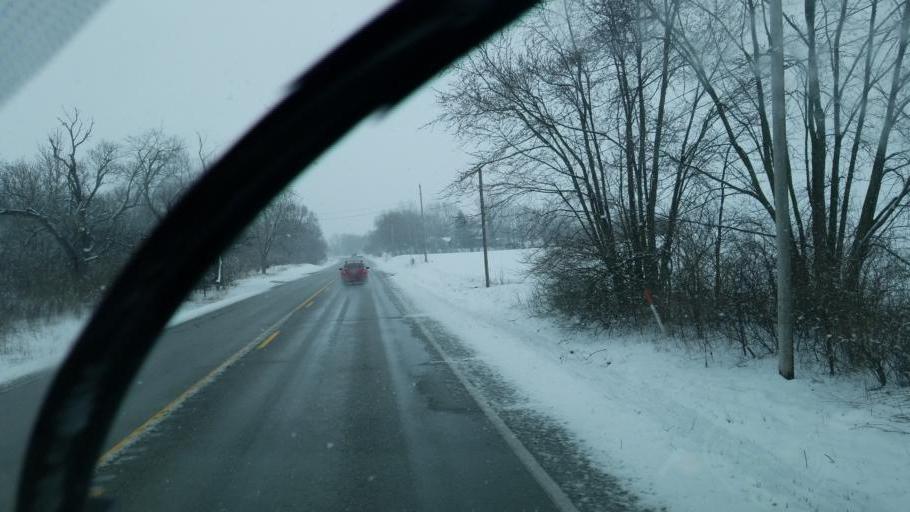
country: US
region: Indiana
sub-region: Randolph County
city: Parker City
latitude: 40.0570
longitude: -85.2378
